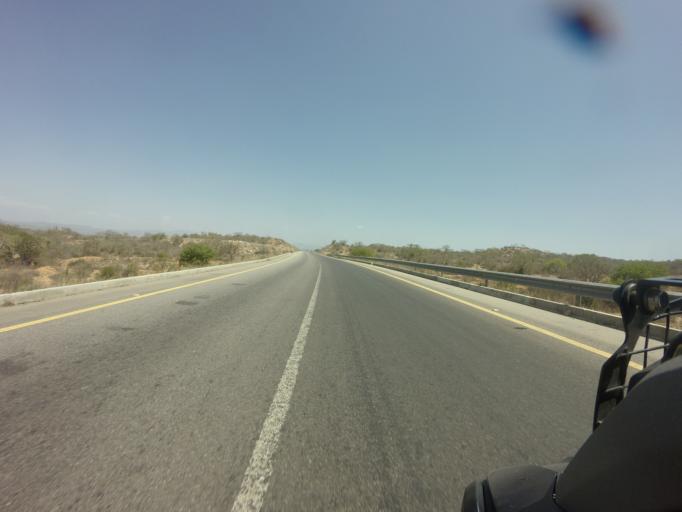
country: AO
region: Benguela
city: Benguela
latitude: -12.9740
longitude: 13.6049
